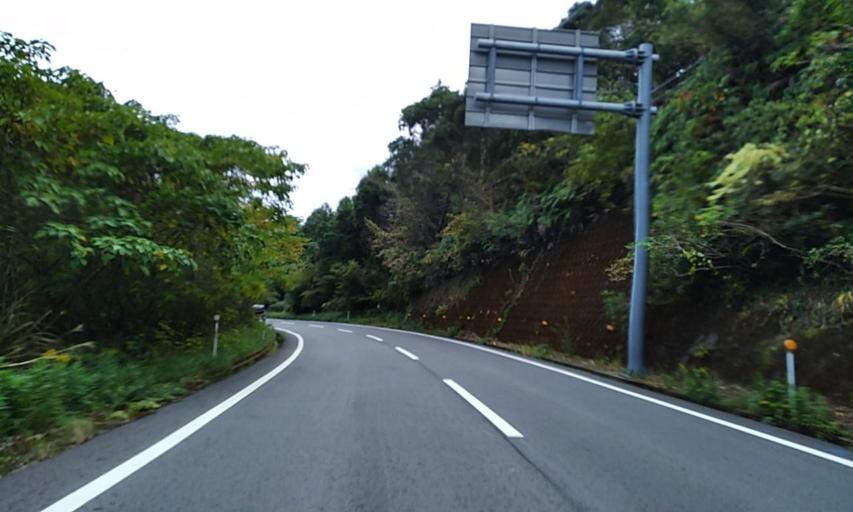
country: JP
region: Wakayama
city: Shingu
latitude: 33.4708
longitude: 135.8187
